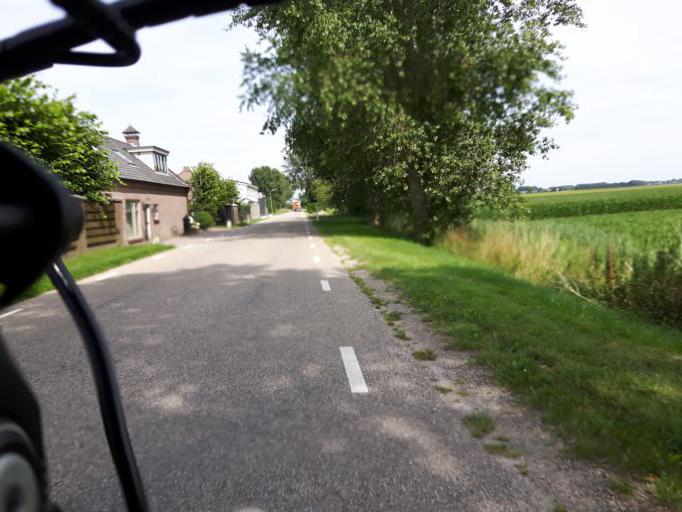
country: NL
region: North Brabant
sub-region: Gemeente Bergen op Zoom
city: Lepelstraat
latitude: 51.5893
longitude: 4.2779
